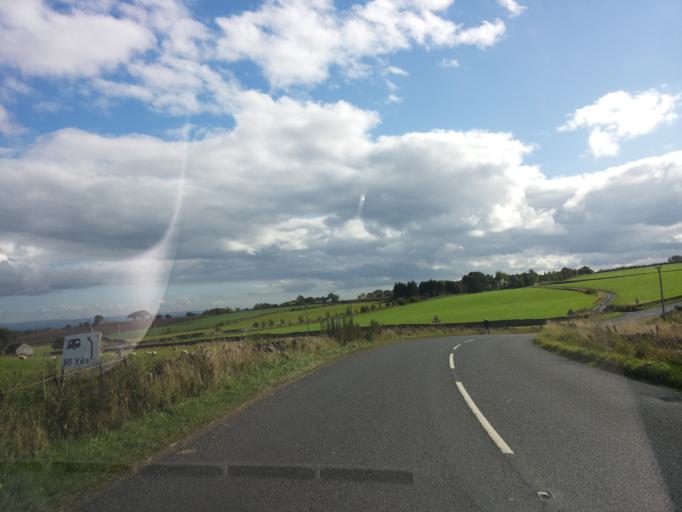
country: GB
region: England
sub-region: North Yorkshire
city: Leyburn
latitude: 54.3242
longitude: -1.8227
